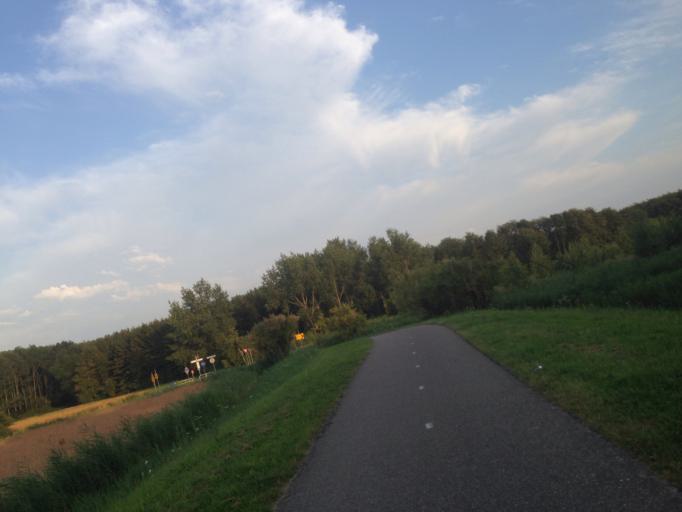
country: NL
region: Flevoland
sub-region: Gemeente Almere
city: Almere Stad
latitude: 52.3863
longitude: 5.2934
